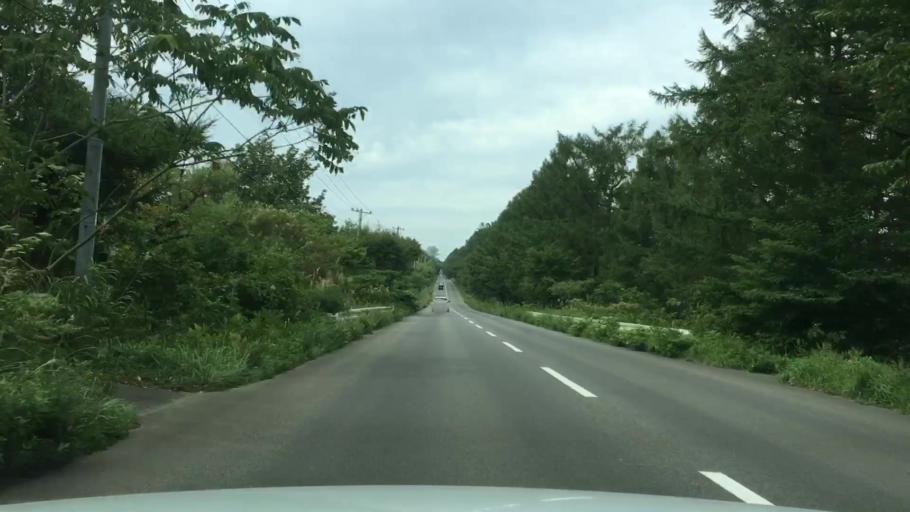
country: JP
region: Aomori
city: Shimokizukuri
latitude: 40.7125
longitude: 140.3262
